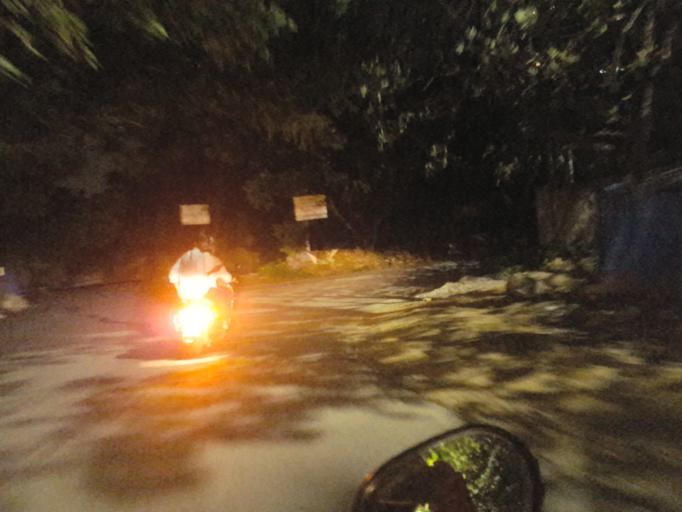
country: IN
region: Telangana
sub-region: Rangareddi
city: Kukatpalli
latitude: 17.4773
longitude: 78.3939
